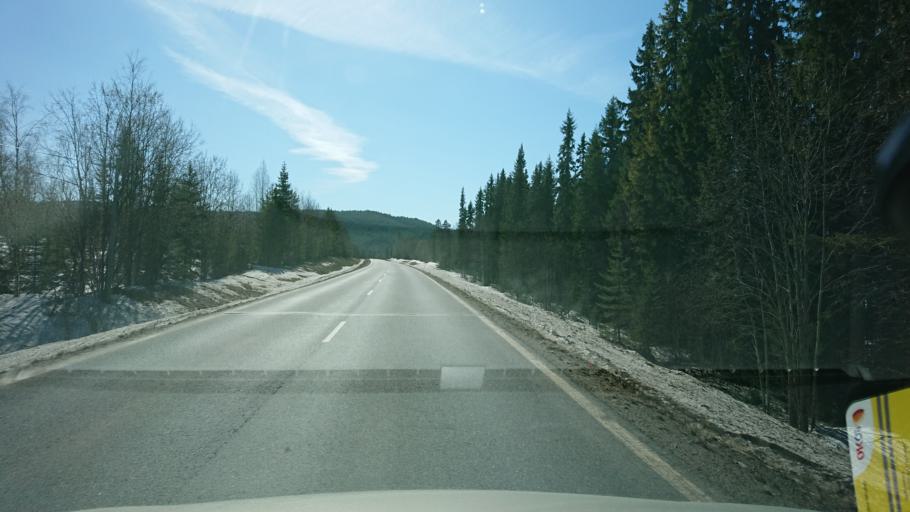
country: SE
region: Vaesterbotten
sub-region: Dorotea Kommun
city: Dorotea
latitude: 64.0643
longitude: 16.2590
